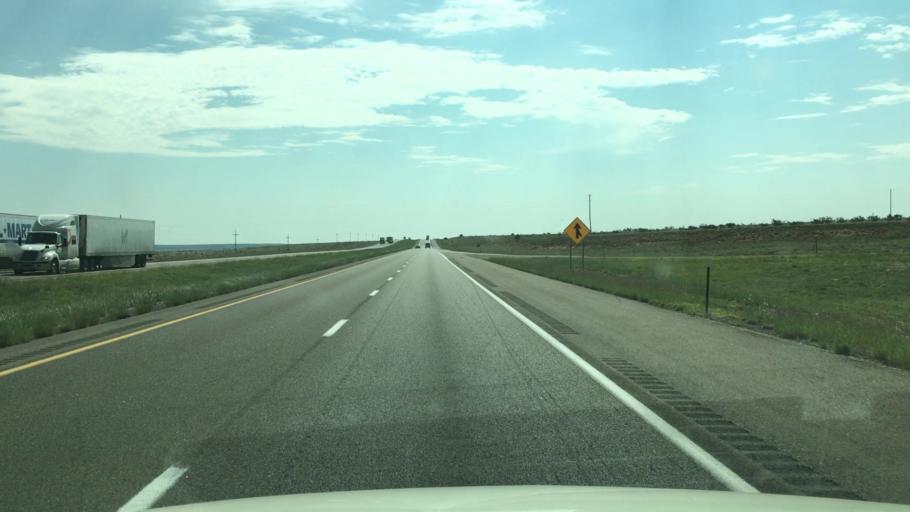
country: US
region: New Mexico
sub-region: Guadalupe County
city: Santa Rosa
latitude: 34.9800
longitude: -105.0653
